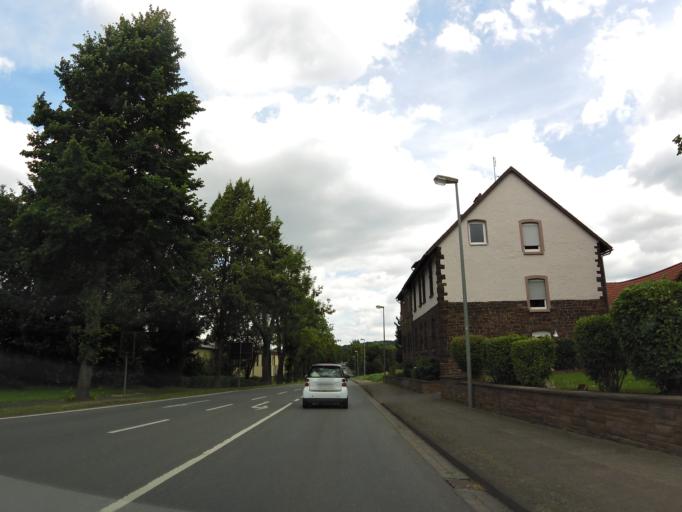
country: DE
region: Lower Saxony
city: Boffzen
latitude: 51.7546
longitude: 9.4001
